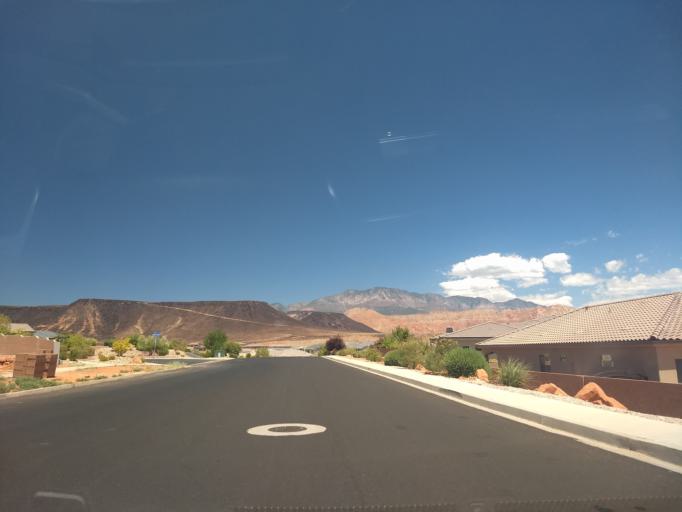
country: US
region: Utah
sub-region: Washington County
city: Washington
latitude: 37.1536
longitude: -113.5309
